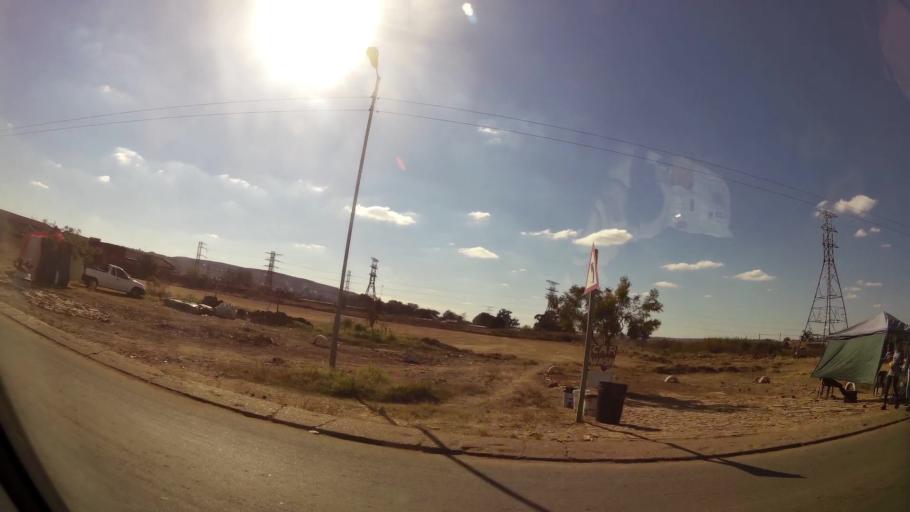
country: ZA
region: Gauteng
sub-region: City of Tshwane Metropolitan Municipality
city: Cullinan
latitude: -25.7139
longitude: 28.3974
